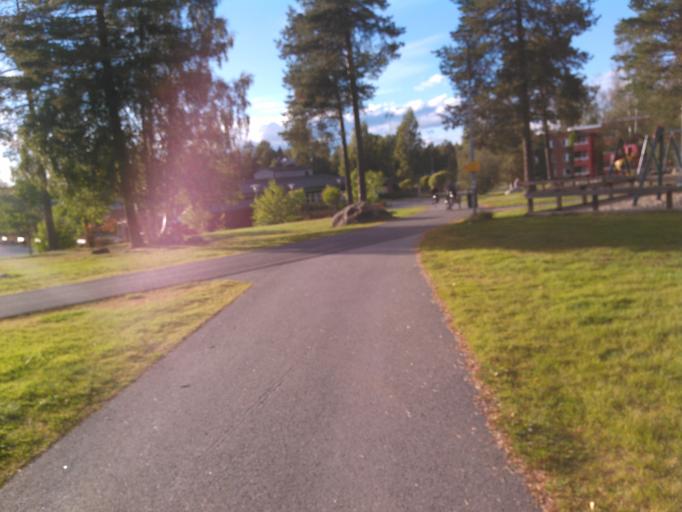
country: SE
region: Vaesterbotten
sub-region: Umea Kommun
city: Umea
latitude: 63.8085
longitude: 20.3177
